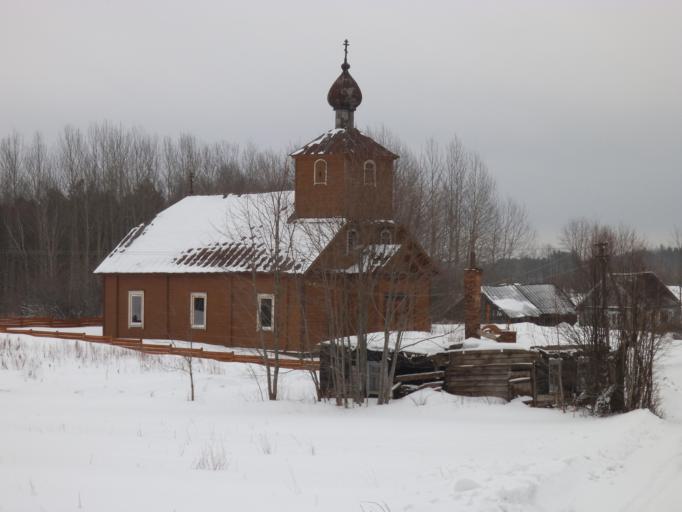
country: LT
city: Zarasai
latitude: 55.6803
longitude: 26.0731
